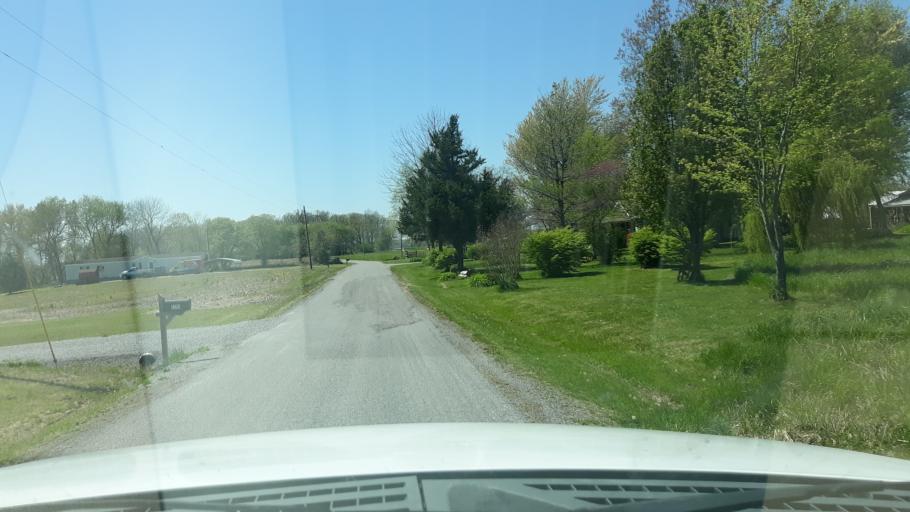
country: US
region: Illinois
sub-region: Saline County
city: Harrisburg
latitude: 37.8849
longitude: -88.6587
